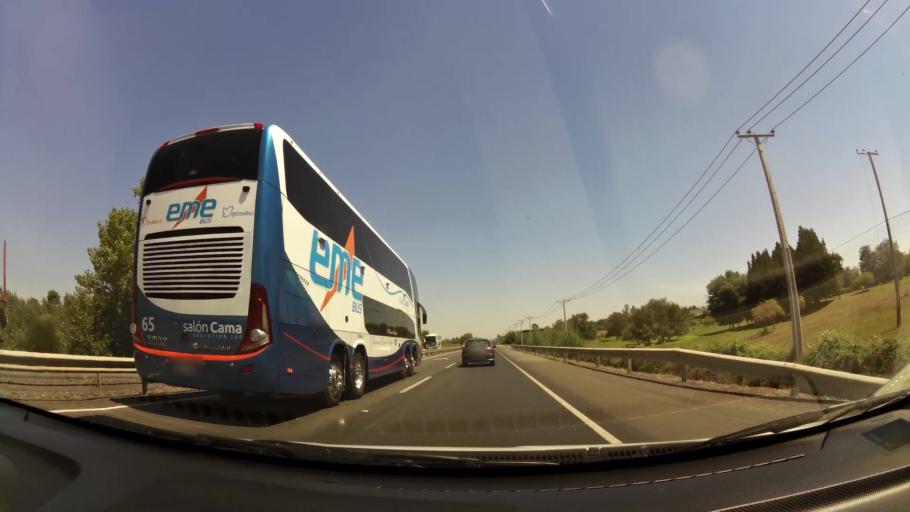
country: CL
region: Maule
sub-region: Provincia de Curico
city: Molina
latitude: -35.2386
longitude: -71.4522
